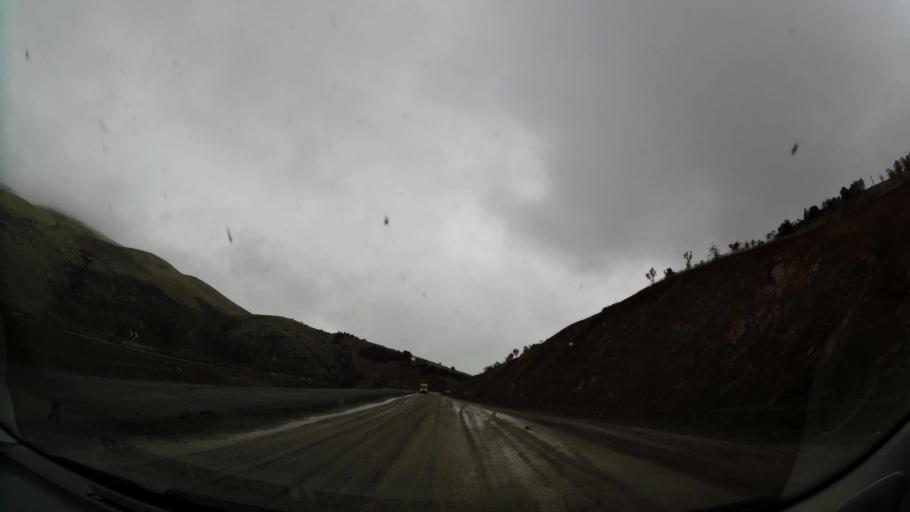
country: MA
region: Taza-Al Hoceima-Taounate
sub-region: Taza
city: Ajdir
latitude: 34.9061
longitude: -3.7937
